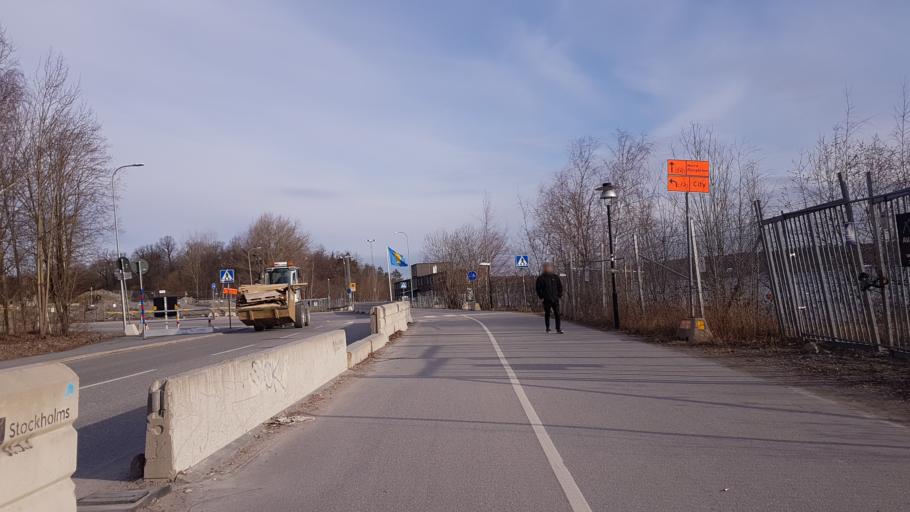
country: SE
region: Stockholm
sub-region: Stockholms Kommun
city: OEstermalm
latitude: 59.3594
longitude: 18.0994
